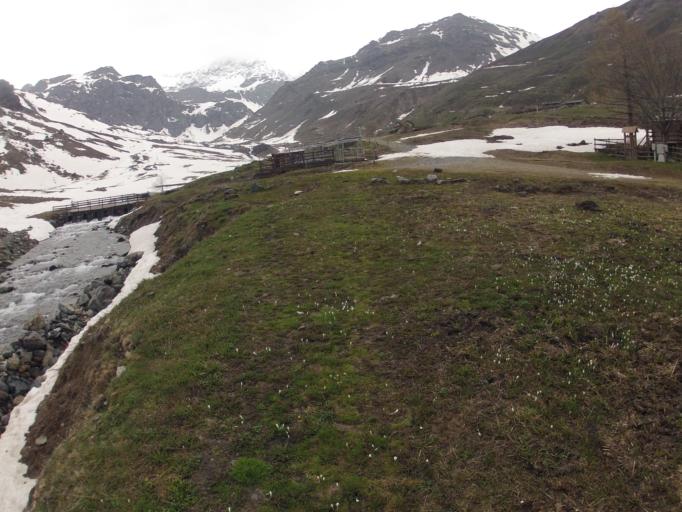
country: IT
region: Piedmont
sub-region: Provincia di Cuneo
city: Crissolo
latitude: 44.6995
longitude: 7.1199
